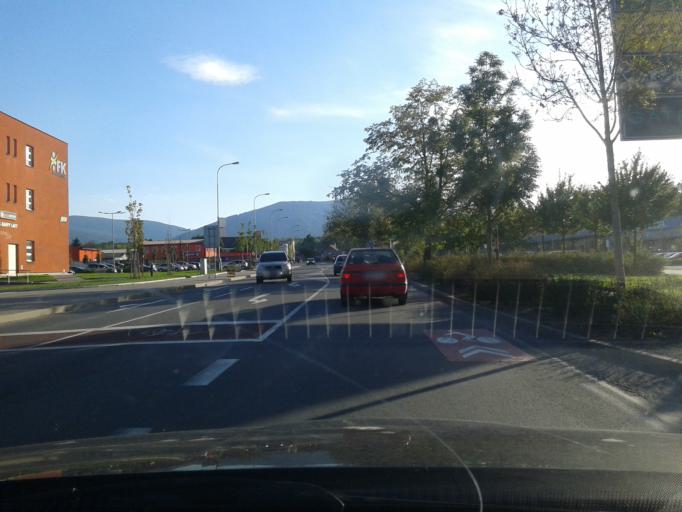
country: CZ
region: Moravskoslezsky
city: Trinec
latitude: 49.6745
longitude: 18.6617
